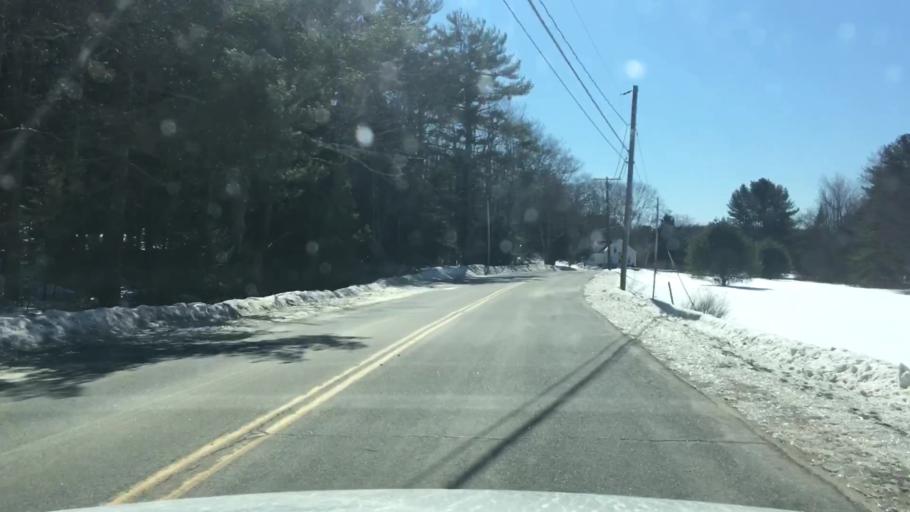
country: US
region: Maine
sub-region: Cumberland County
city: Brunswick
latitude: 43.8673
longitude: -70.0166
